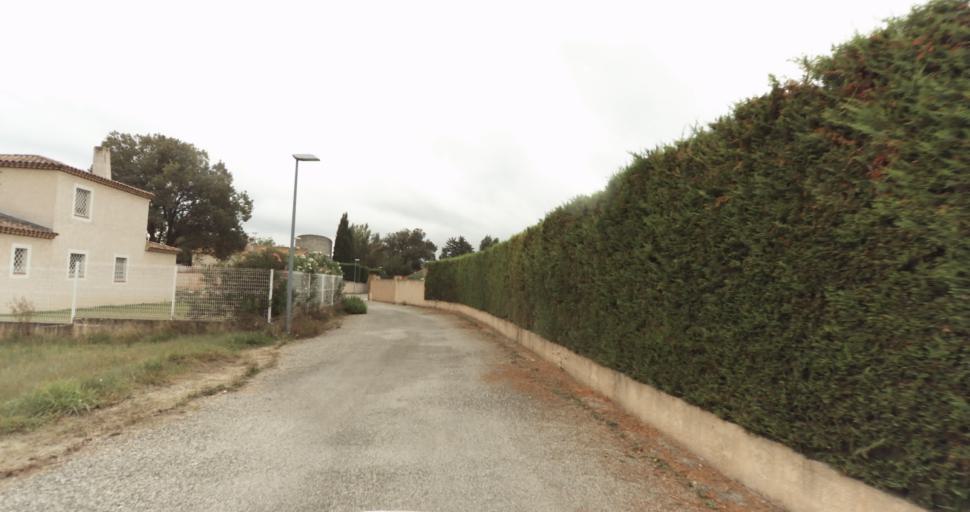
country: FR
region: Provence-Alpes-Cote d'Azur
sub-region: Departement des Bouches-du-Rhone
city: Saint-Victoret
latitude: 43.4200
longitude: 5.2545
